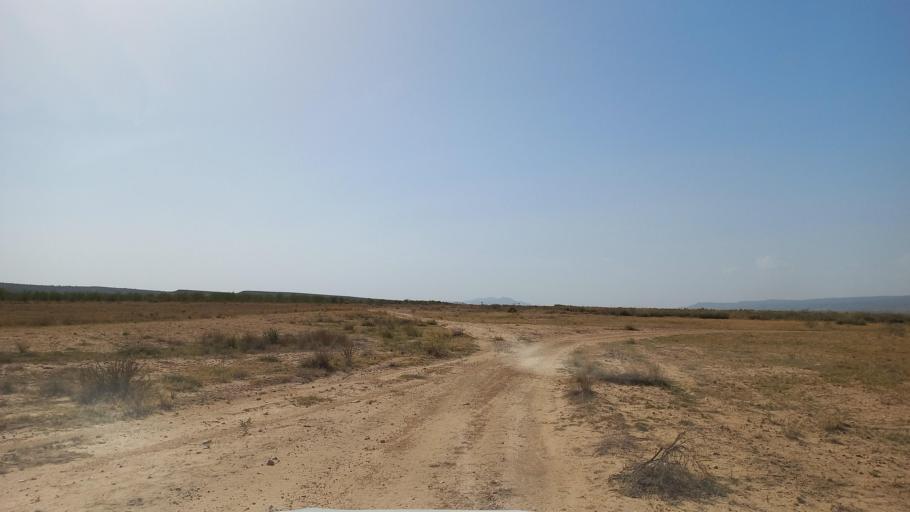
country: TN
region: Al Qasrayn
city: Kasserine
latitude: 35.2140
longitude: 9.0271
